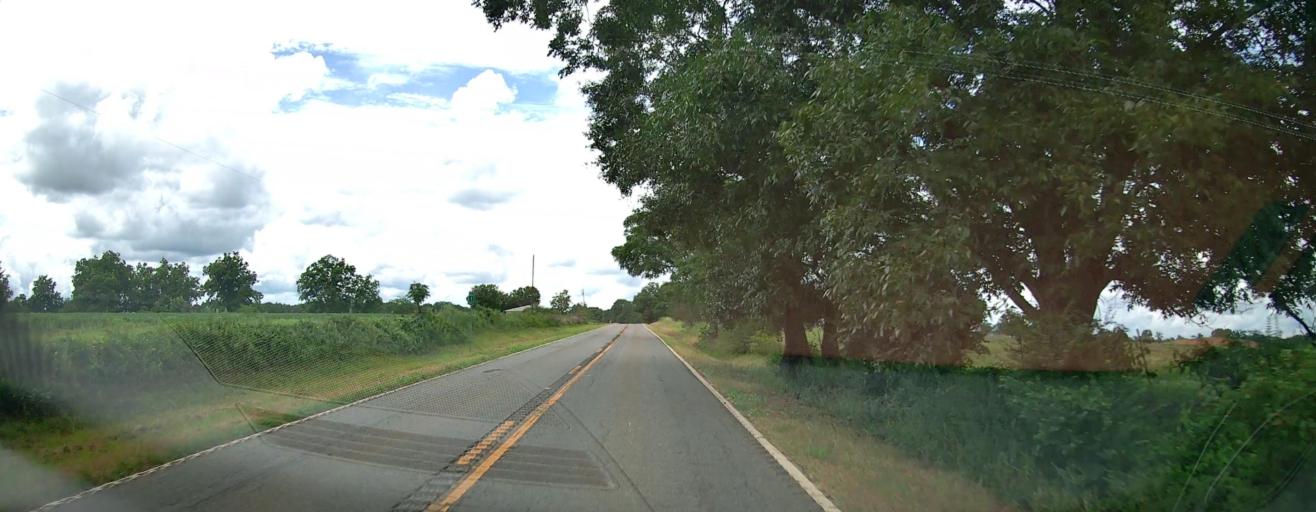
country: US
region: Georgia
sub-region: Macon County
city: Montezuma
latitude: 32.2944
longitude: -83.9000
